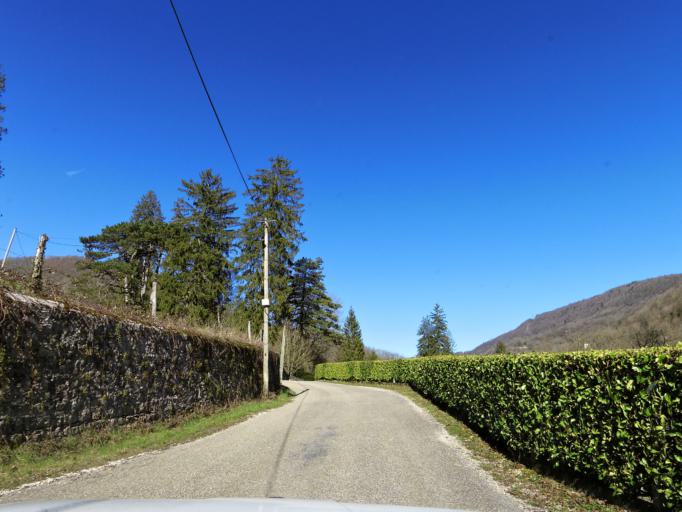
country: FR
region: Rhone-Alpes
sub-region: Departement de l'Ain
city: Saint-Rambert-en-Bugey
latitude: 45.9500
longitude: 5.4345
